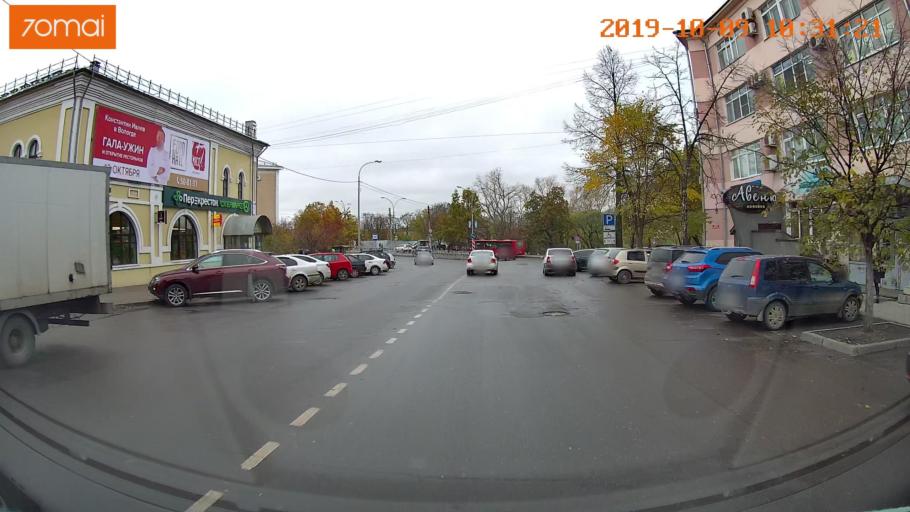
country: RU
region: Vologda
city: Vologda
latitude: 59.2216
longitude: 39.8932
